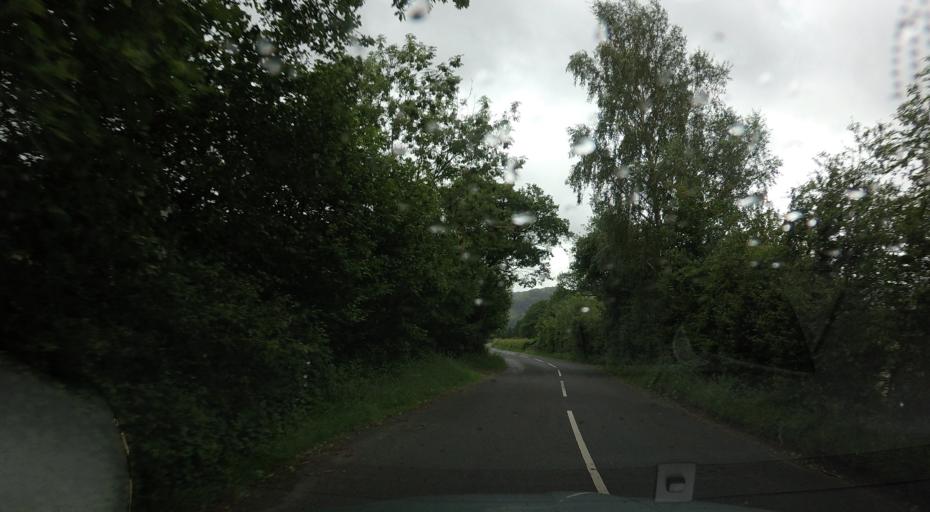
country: GB
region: England
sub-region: Cumbria
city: Keswick
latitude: 54.5272
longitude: -3.1508
